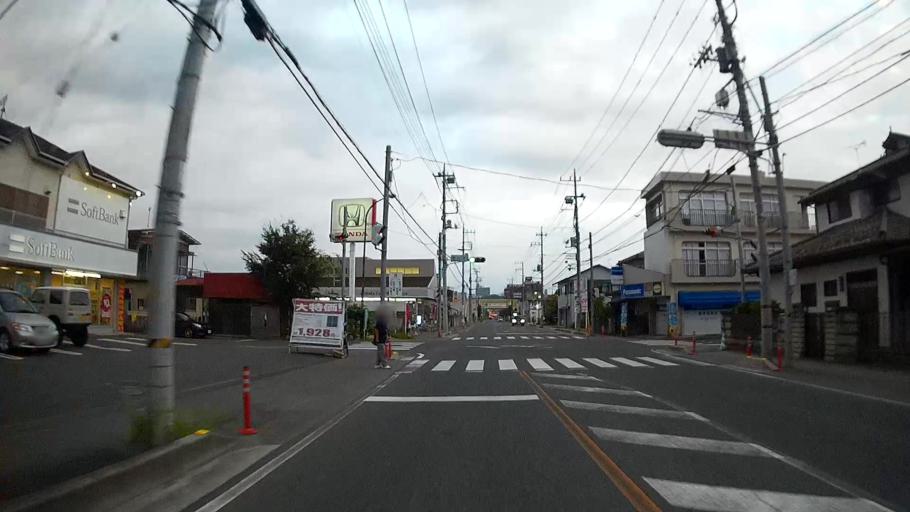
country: JP
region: Saitama
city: Chichibu
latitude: 35.9855
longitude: 139.0823
